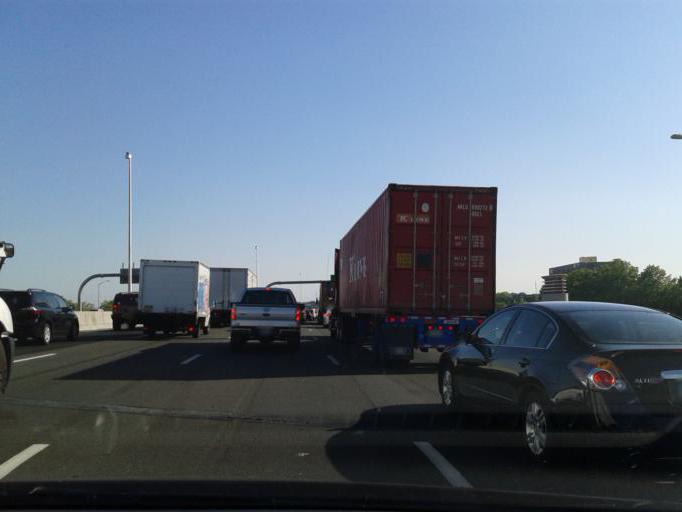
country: US
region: Connecticut
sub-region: New Haven County
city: New Haven
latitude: 41.2965
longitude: -72.9171
